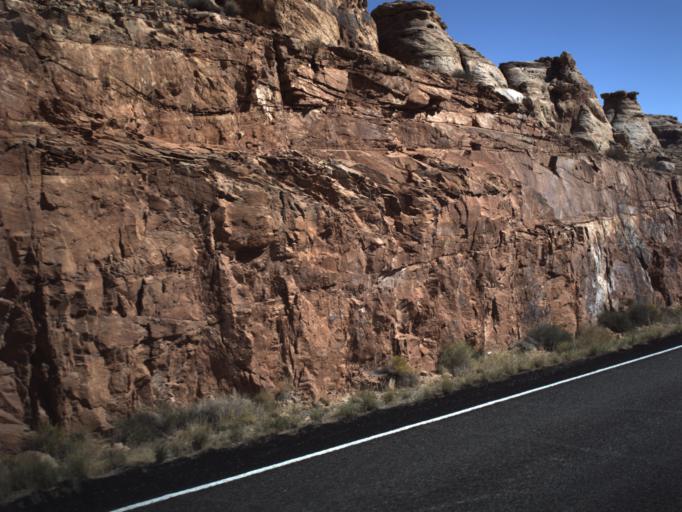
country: US
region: Utah
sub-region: San Juan County
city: Blanding
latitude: 37.8944
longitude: -110.3750
